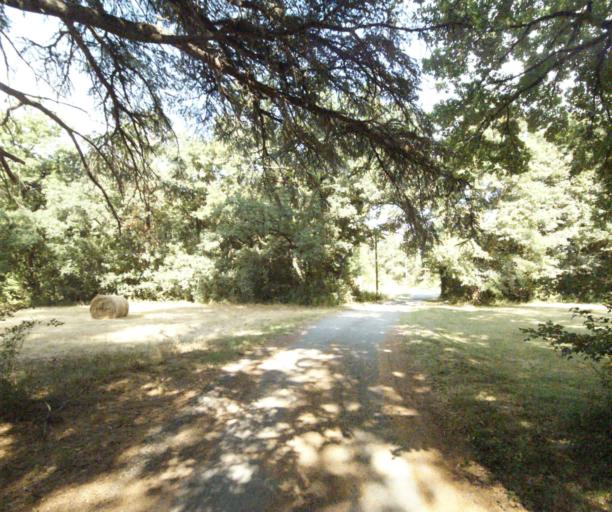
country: FR
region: Midi-Pyrenees
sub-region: Departement du Tarn
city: Soual
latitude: 43.5227
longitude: 2.0933
